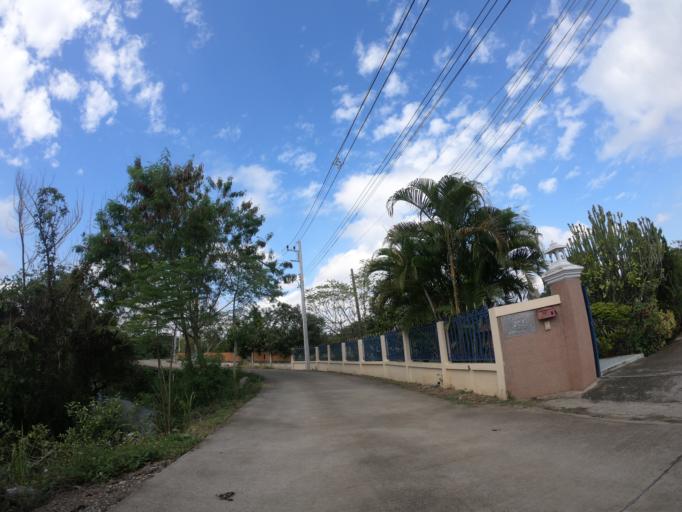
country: TH
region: Chiang Mai
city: Saraphi
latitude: 18.7013
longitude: 98.9792
